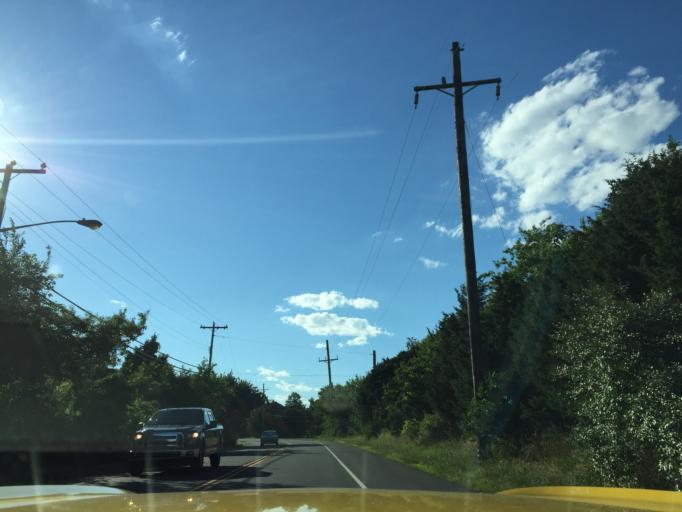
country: US
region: New York
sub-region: Suffolk County
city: Greenport
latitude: 41.1494
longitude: -72.2659
